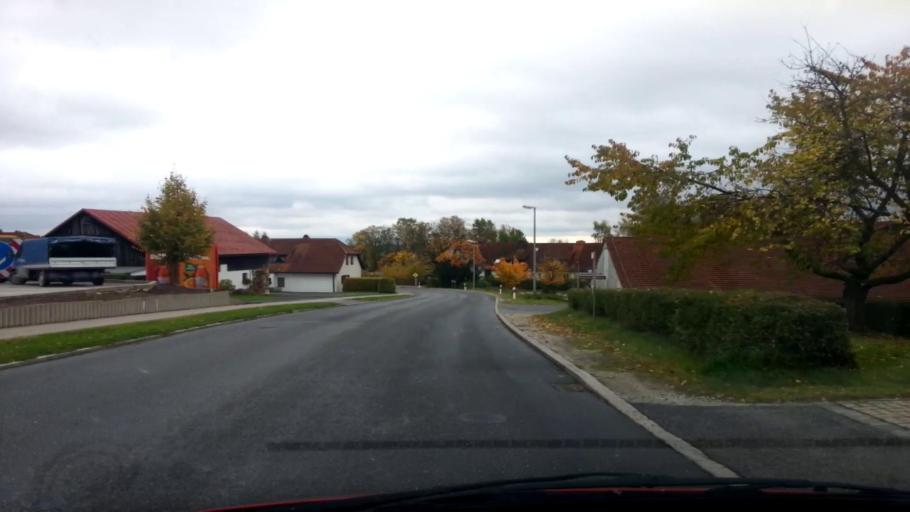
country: DE
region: Bavaria
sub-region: Upper Franconia
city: Fichtelberg
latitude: 49.9999
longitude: 11.8461
